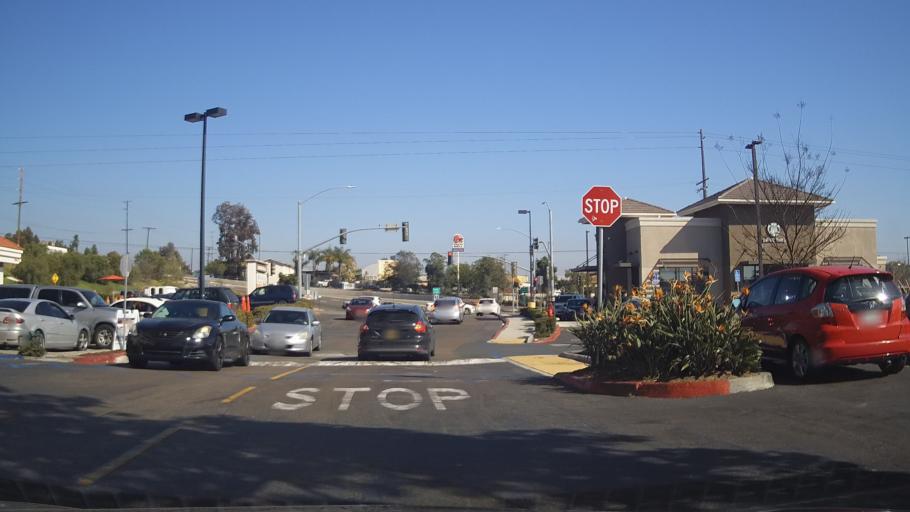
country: US
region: California
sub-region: San Diego County
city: Lemon Grove
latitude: 32.7438
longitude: -117.0438
